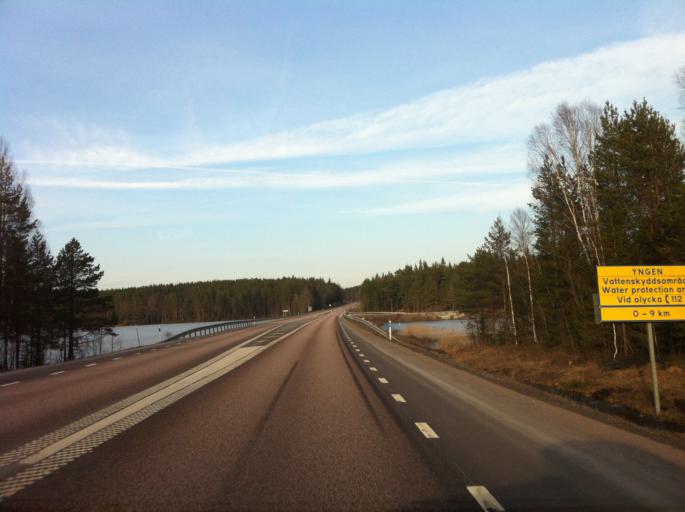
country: SE
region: Vaermland
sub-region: Filipstads Kommun
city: Filipstad
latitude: 59.7345
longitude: 14.2220
